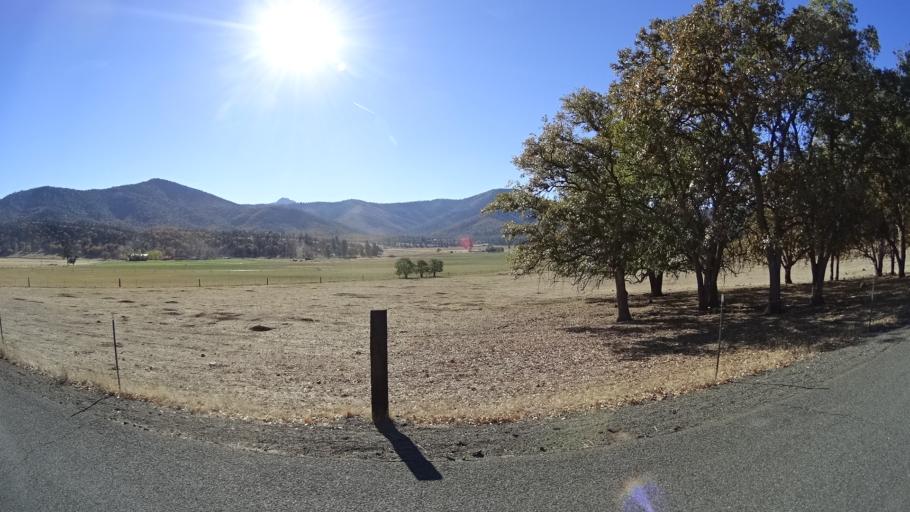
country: US
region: California
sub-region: Siskiyou County
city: Yreka
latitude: 41.5810
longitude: -122.7960
